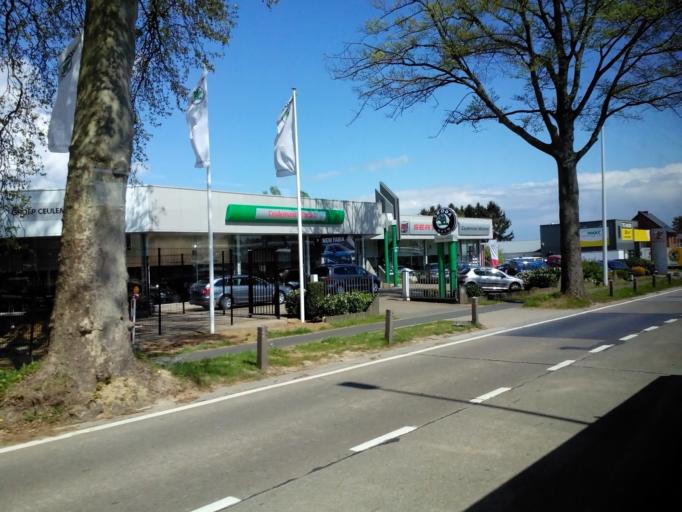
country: BE
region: Flanders
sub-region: Provincie Vlaams-Brabant
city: Herent
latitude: 50.8876
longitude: 4.6635
